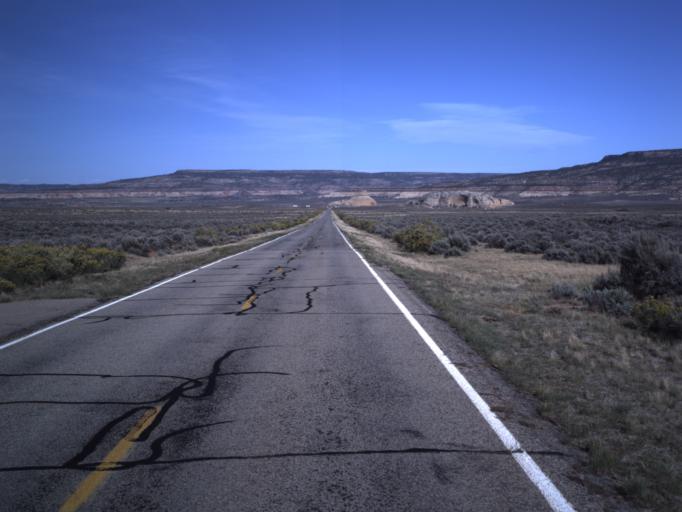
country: US
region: Utah
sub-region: San Juan County
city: Monticello
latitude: 38.0627
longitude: -109.3932
